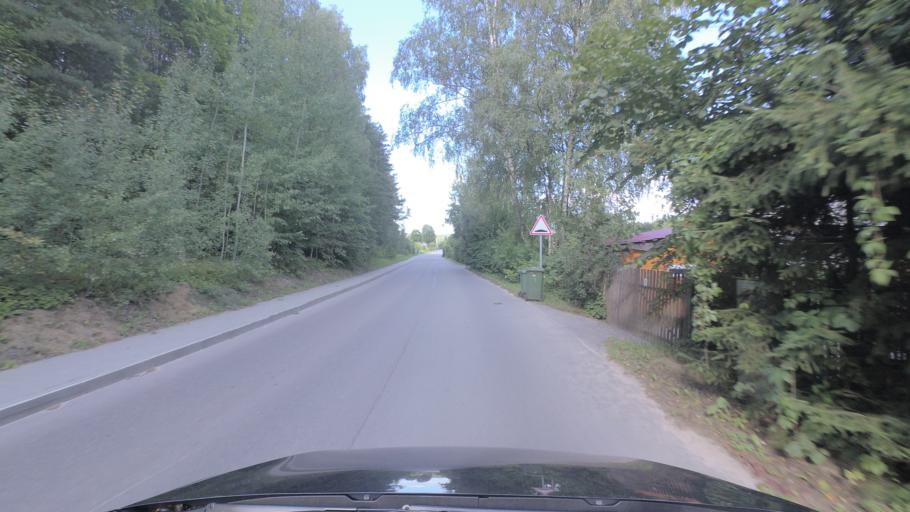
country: LT
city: Nemencine
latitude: 54.8532
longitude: 25.3765
